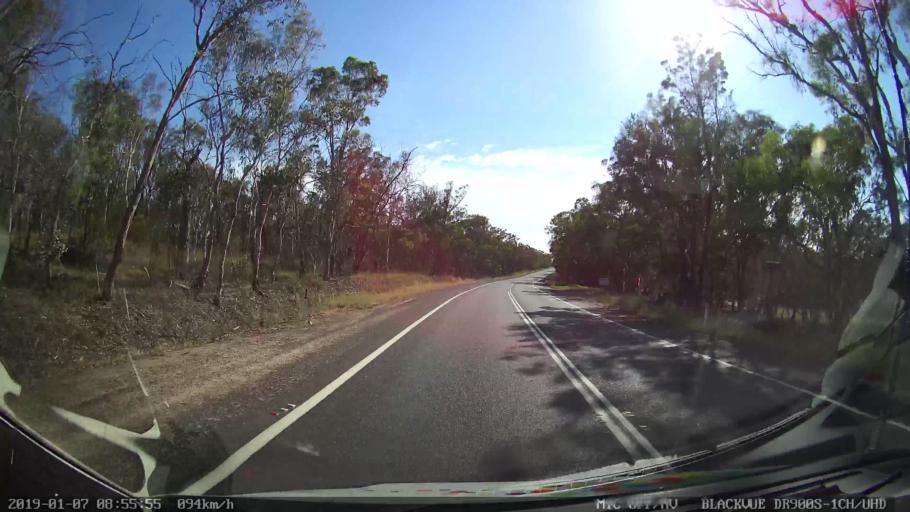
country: AU
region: New South Wales
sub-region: Tamworth Municipality
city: Kootingal
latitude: -30.7809
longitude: 151.3353
